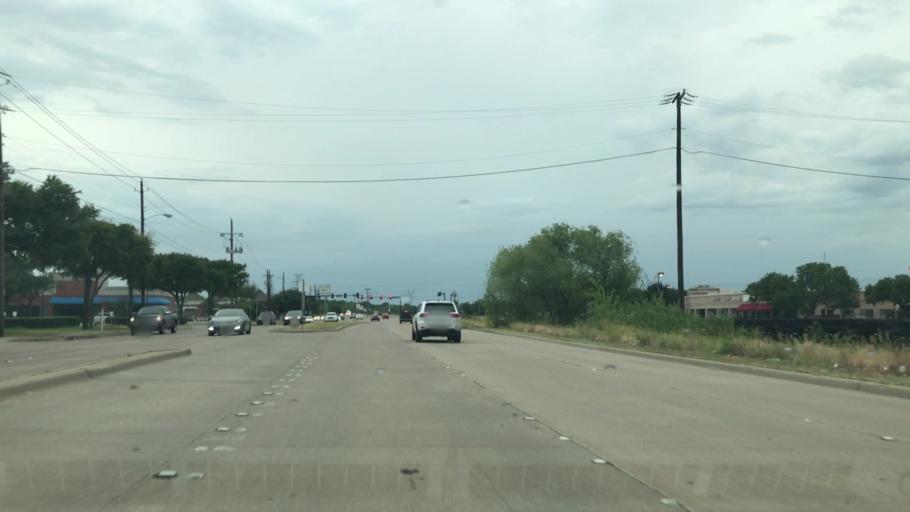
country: US
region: Texas
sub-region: Dallas County
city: Coppell
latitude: 32.9526
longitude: -96.9553
